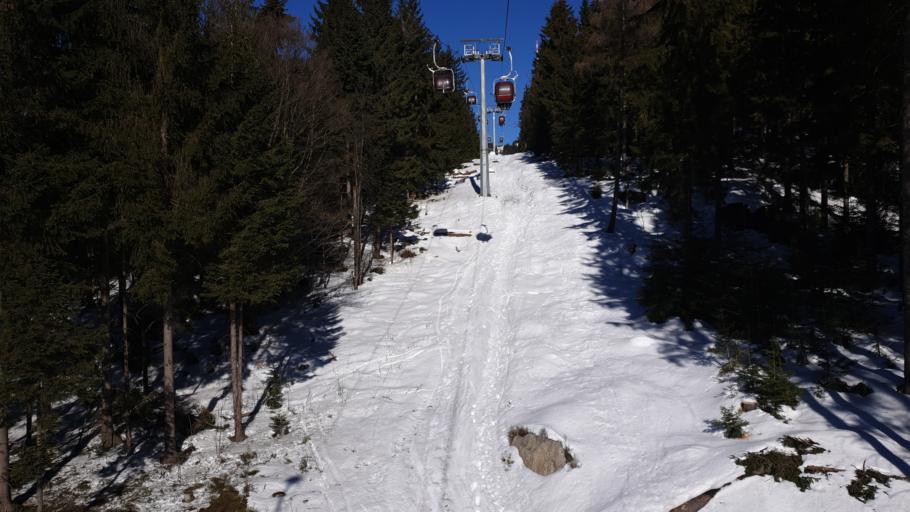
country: DE
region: Bavaria
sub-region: Upper Franconia
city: Bischofsgrun
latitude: 50.0180
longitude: 11.8084
